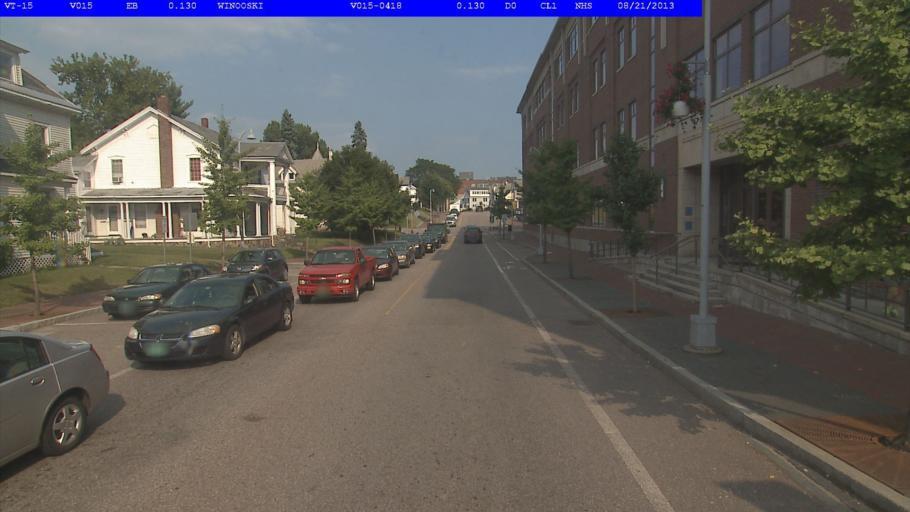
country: US
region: Vermont
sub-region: Chittenden County
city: Winooski
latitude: 44.4913
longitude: -73.1854
